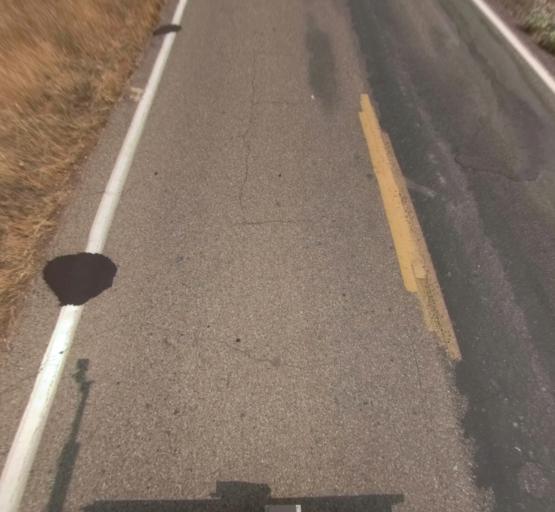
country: US
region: California
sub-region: Madera County
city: Yosemite Lakes
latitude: 37.2060
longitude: -119.9082
